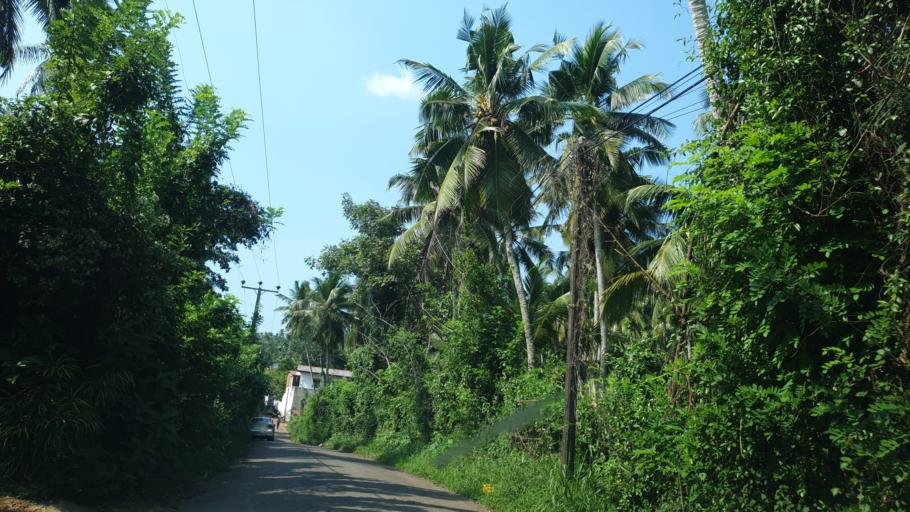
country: LK
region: Western
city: Moratuwa
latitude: 6.7652
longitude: 79.9234
